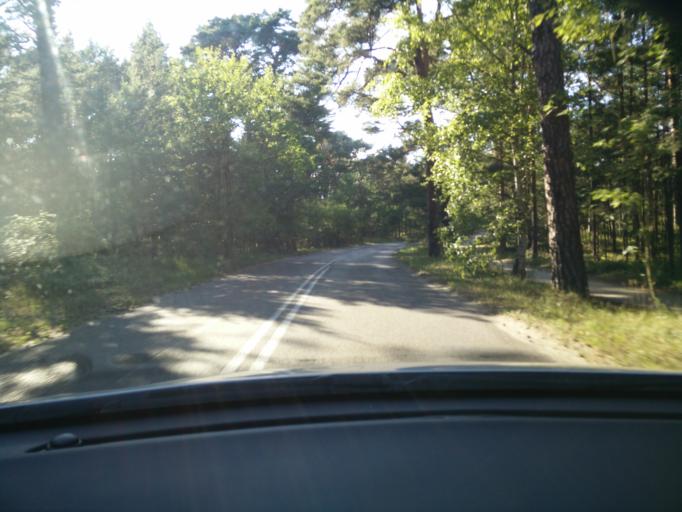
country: PL
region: Pomeranian Voivodeship
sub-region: Powiat pucki
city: Jastarnia
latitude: 54.6714
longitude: 18.7334
